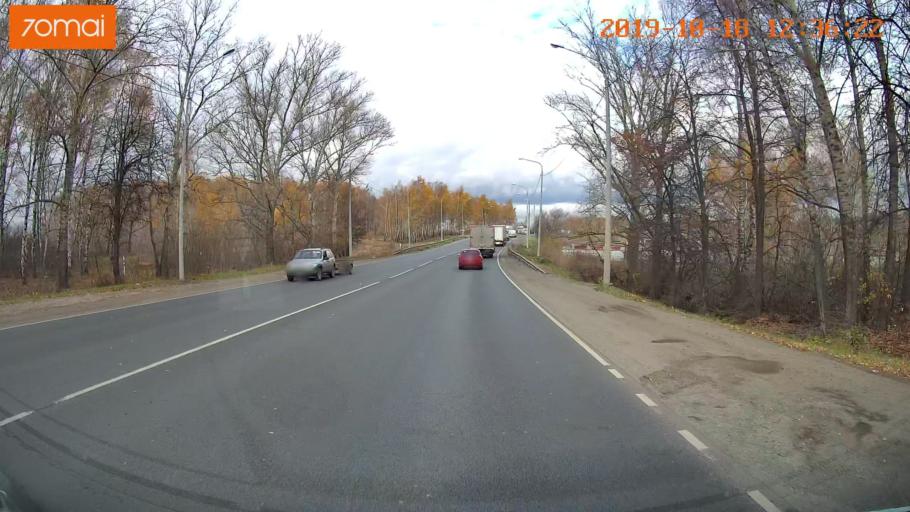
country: RU
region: Rjazan
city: Ryazan'
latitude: 54.6345
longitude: 39.6340
